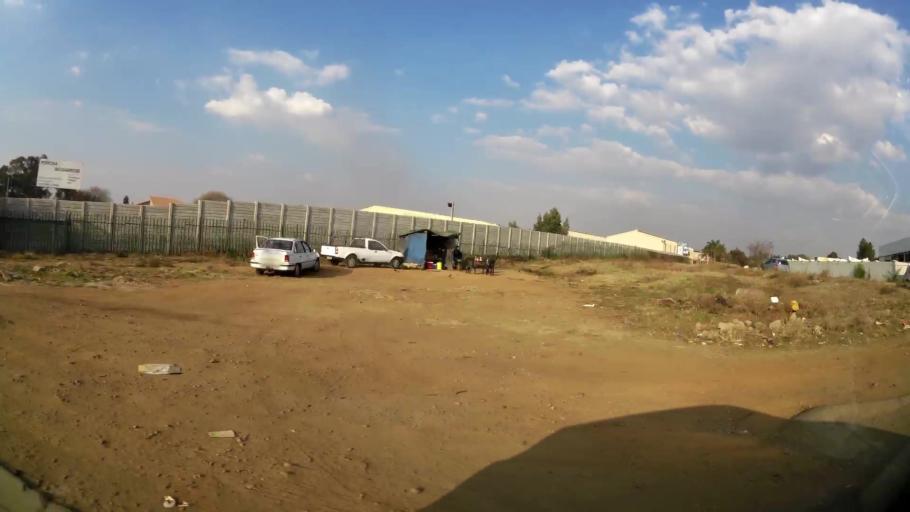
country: ZA
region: Gauteng
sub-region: Ekurhuleni Metropolitan Municipality
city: Benoni
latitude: -26.1120
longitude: 28.2674
